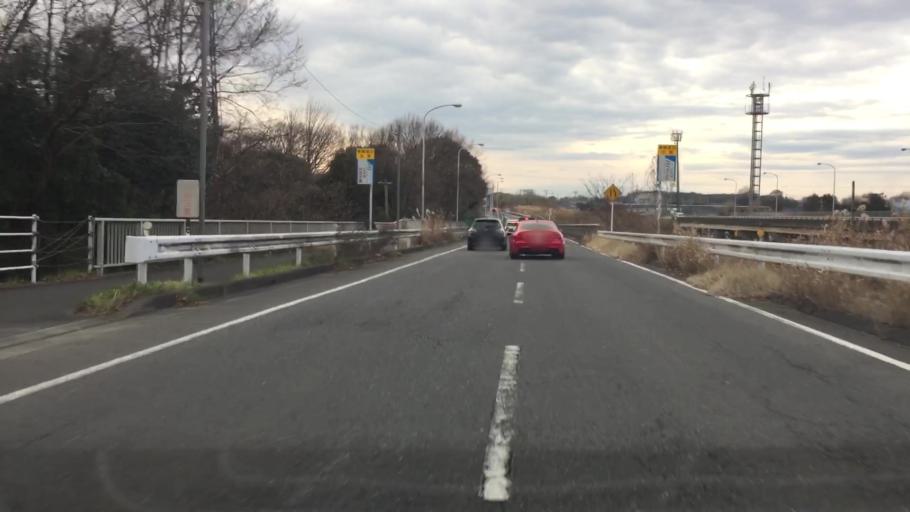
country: JP
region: Chiba
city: Shiroi
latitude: 35.7839
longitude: 140.0085
